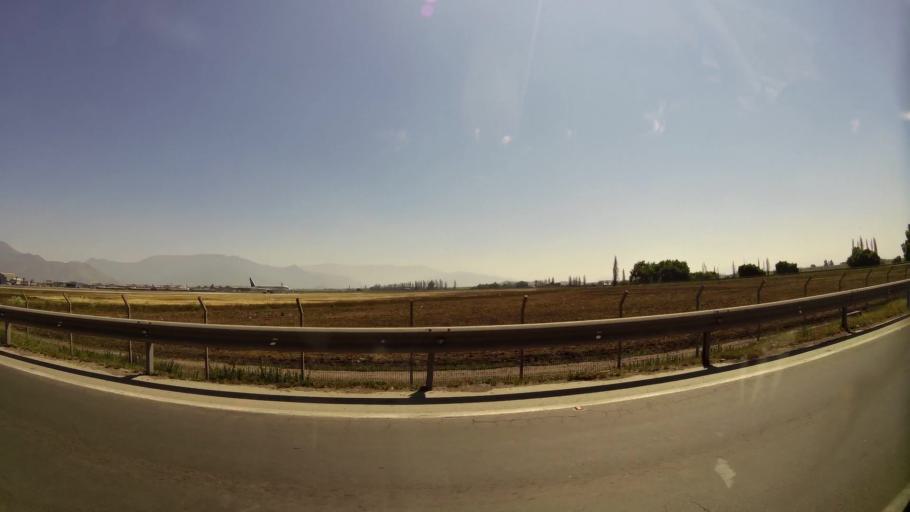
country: CL
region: Santiago Metropolitan
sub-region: Provincia de Santiago
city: Lo Prado
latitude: -33.3781
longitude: -70.7834
